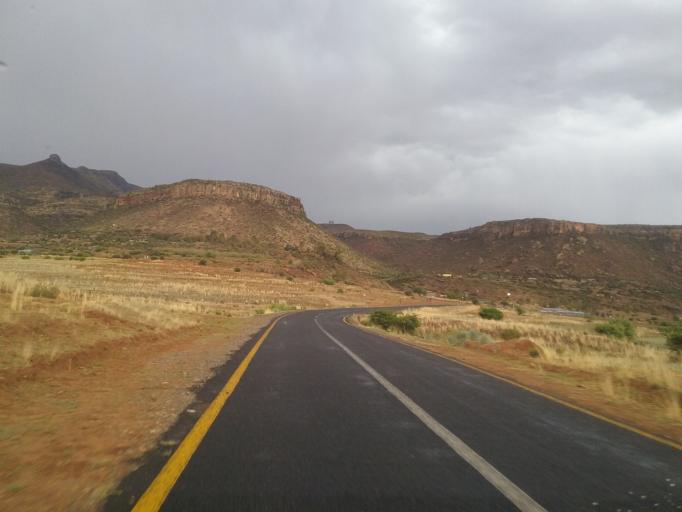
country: LS
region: Quthing
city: Quthing
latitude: -30.3220
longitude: 27.7457
